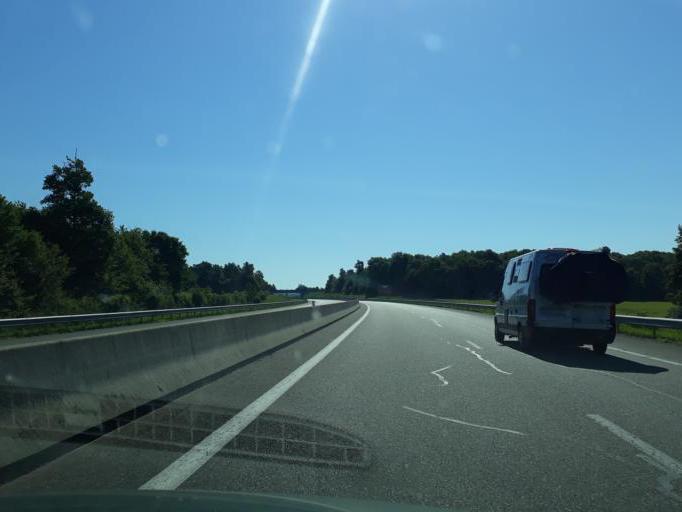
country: FR
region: Centre
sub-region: Departement du Loiret
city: Saint-Germain-des-Pres
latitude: 48.0442
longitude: 2.8926
